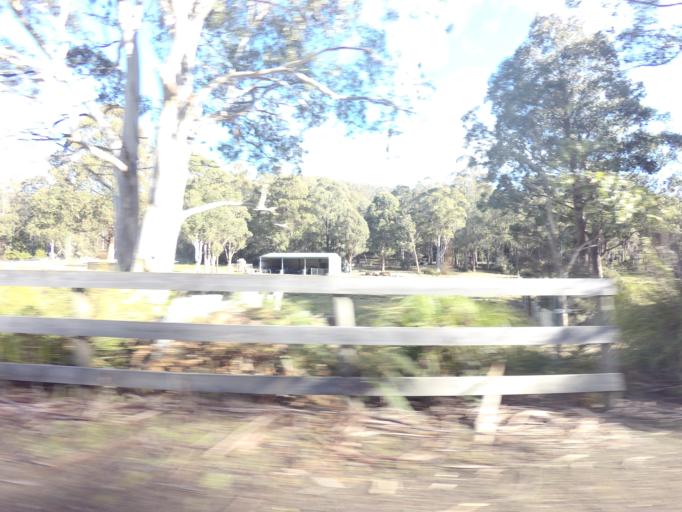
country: AU
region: Tasmania
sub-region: Glenorchy
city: Berriedale
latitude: -42.8435
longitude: 147.1662
